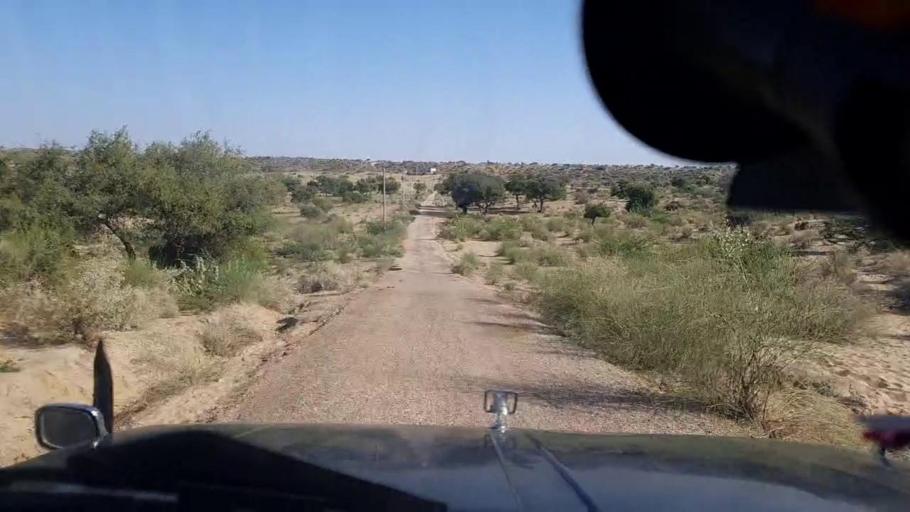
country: PK
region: Sindh
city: Diplo
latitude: 24.4702
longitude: 69.8053
